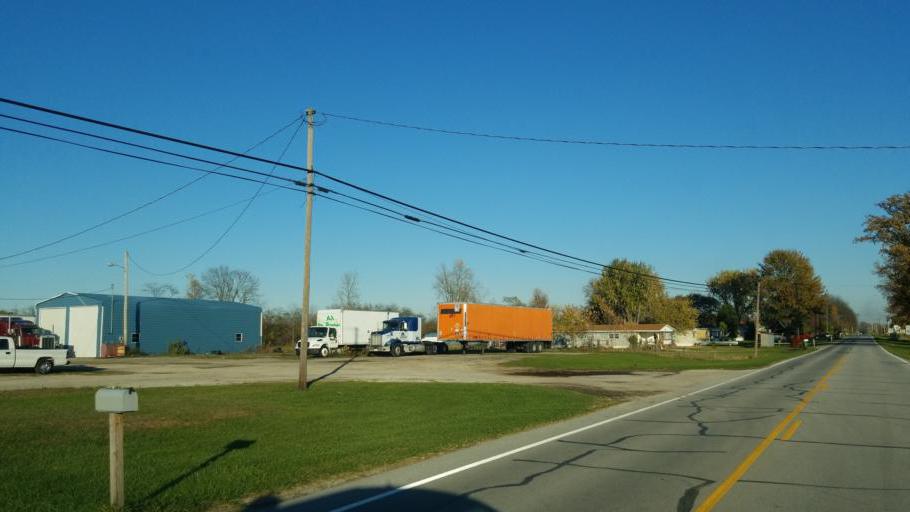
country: US
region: Ohio
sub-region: Sandusky County
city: Stony Prairie
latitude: 41.3278
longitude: -83.1673
